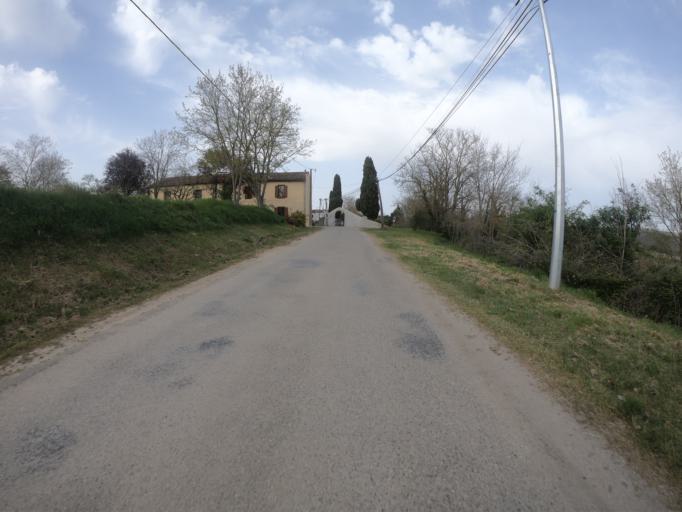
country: FR
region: Languedoc-Roussillon
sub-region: Departement de l'Aude
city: Belpech
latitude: 43.1454
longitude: 1.7138
